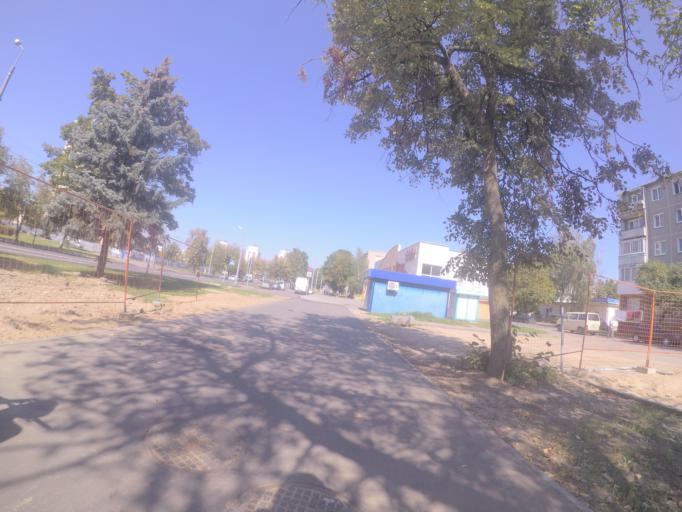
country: BY
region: Grodnenskaya
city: Hrodna
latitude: 53.6693
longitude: 23.8027
